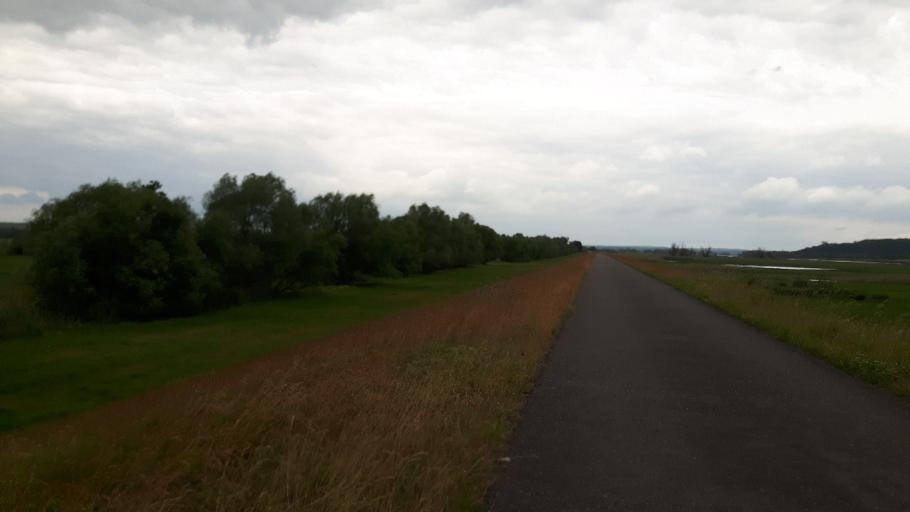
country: PL
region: West Pomeranian Voivodeship
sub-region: Powiat gryfinski
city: Cedynia
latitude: 52.9108
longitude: 14.1457
